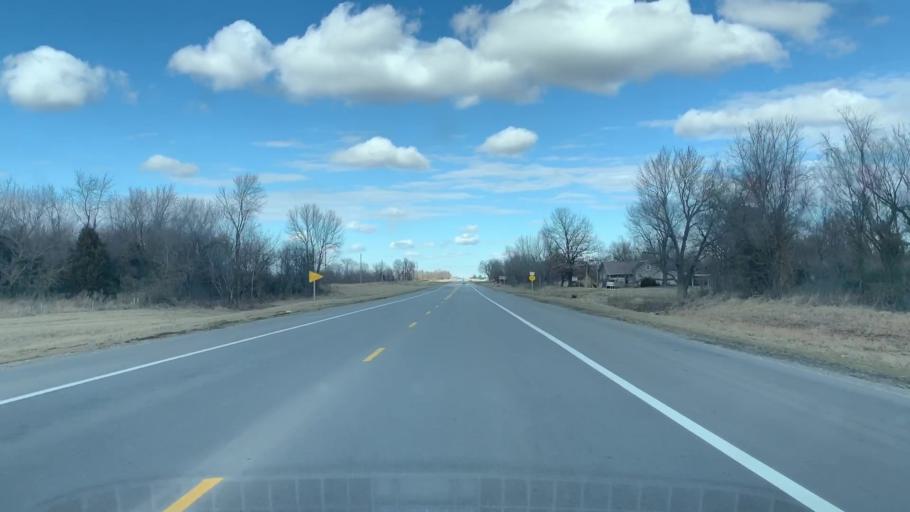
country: US
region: Kansas
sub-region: Cherokee County
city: Columbus
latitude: 37.2754
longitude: -94.8321
